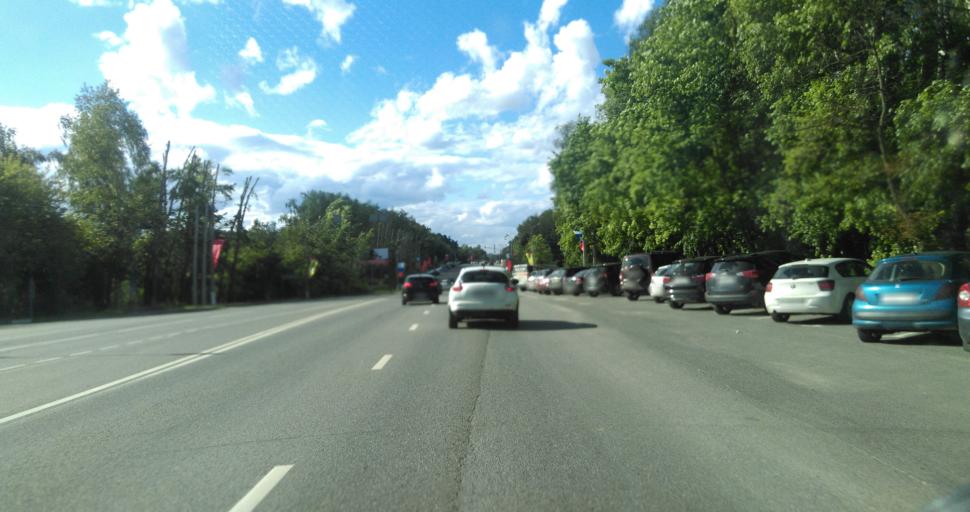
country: RU
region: Moskovskaya
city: Vostryakovo
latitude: 55.4163
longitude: 37.7797
